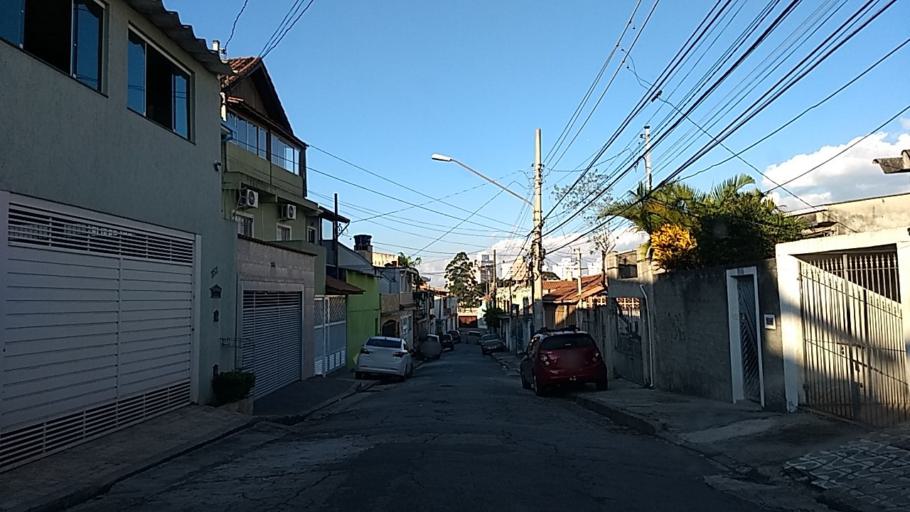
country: BR
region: Sao Paulo
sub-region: Sao Paulo
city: Sao Paulo
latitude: -23.4923
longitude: -46.6055
